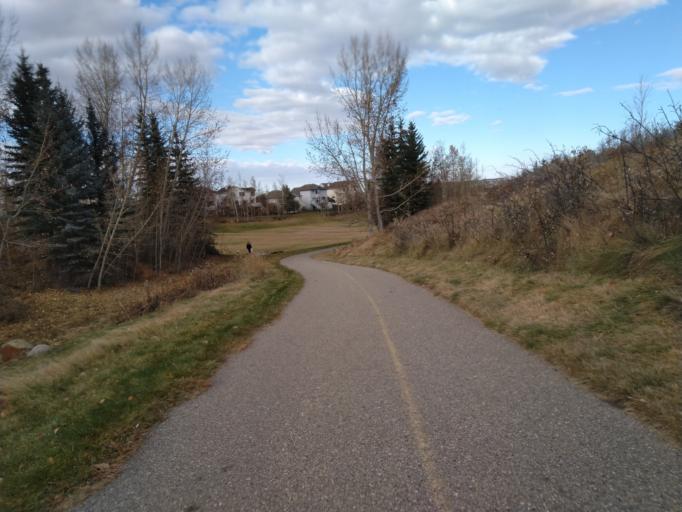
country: CA
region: Alberta
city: Calgary
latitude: 51.1479
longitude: -114.1137
